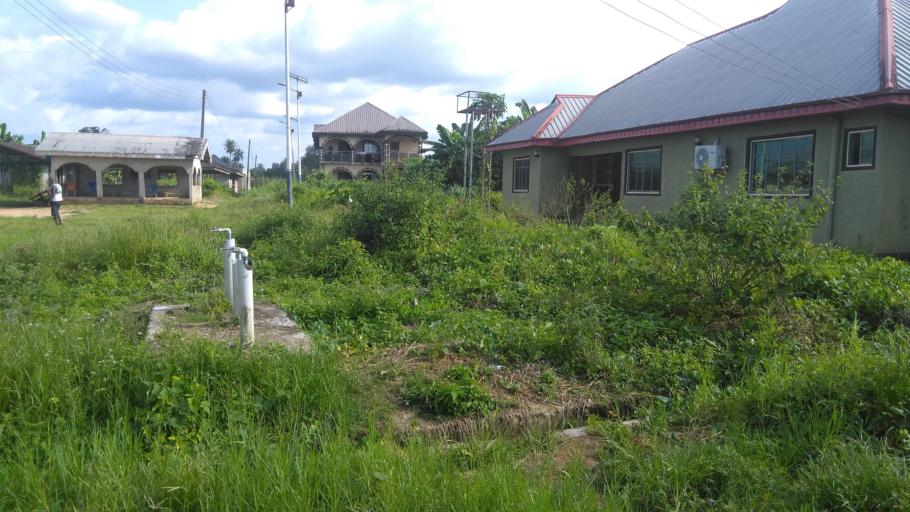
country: NG
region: Edo
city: Siluko
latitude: 6.1439
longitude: 5.1995
